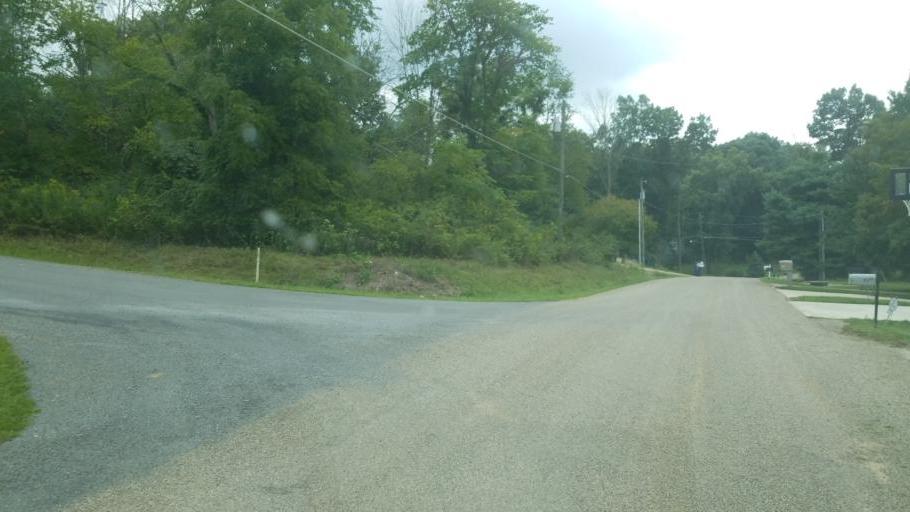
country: US
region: Ohio
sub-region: Knox County
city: Danville
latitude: 40.4529
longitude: -82.3369
